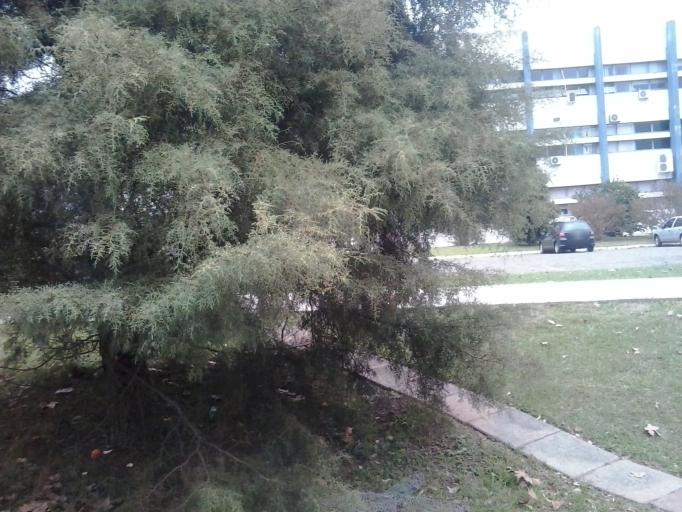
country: BR
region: Rio Grande do Sul
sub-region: Santa Maria
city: Santa Maria
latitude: -29.7187
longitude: -53.7153
